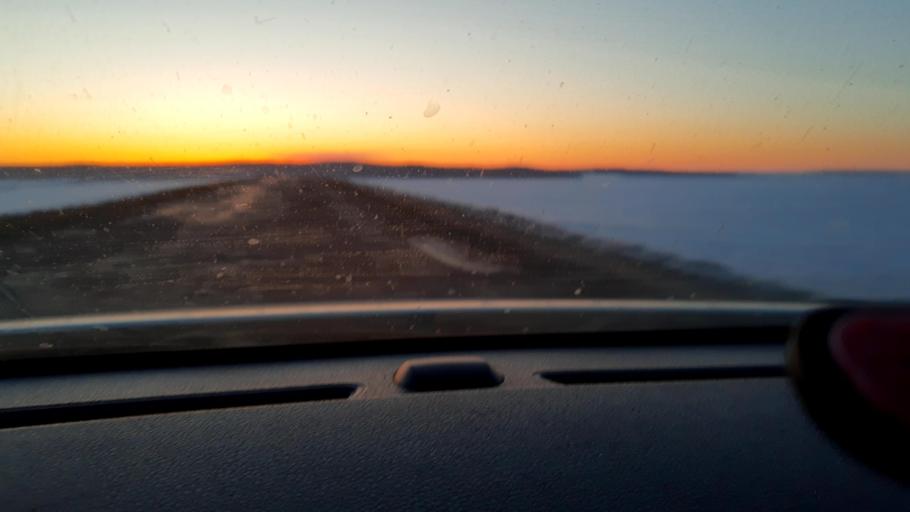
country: RU
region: Bashkortostan
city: Avdon
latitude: 54.3880
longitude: 55.7741
